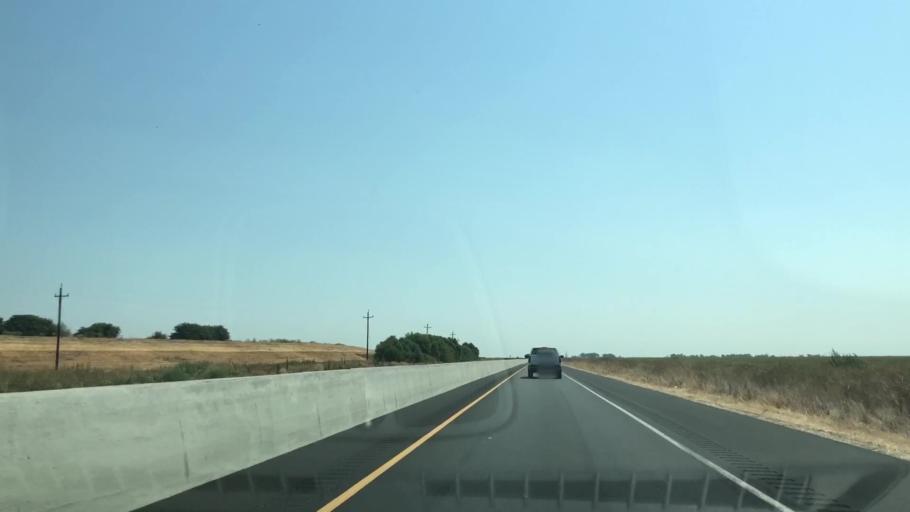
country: US
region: California
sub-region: Contra Costa County
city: Bethel Island
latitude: 38.1173
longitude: -121.5614
